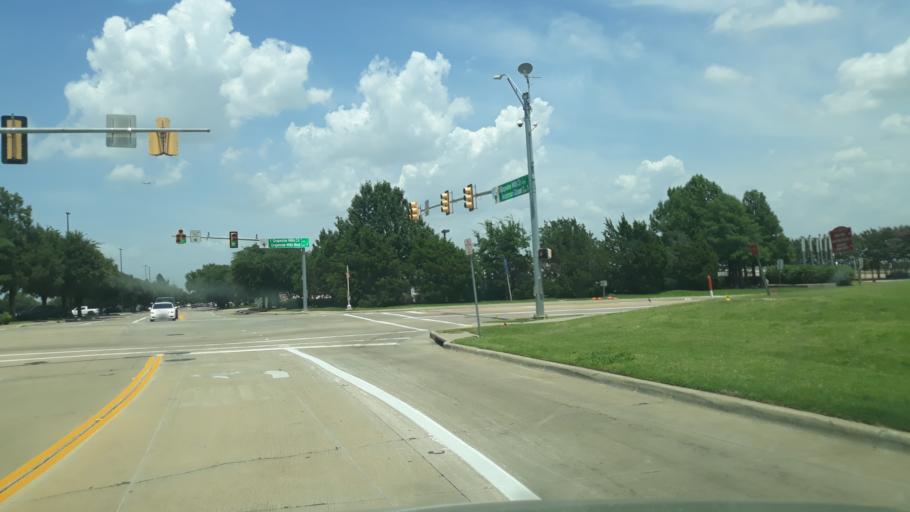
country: US
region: Texas
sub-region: Dallas County
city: Coppell
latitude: 32.9604
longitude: -97.0440
